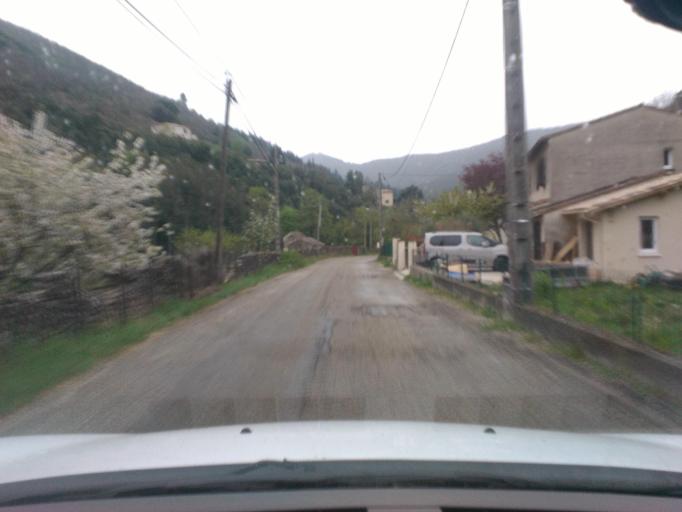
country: FR
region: Languedoc-Roussillon
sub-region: Departement du Gard
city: Valleraugue
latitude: 44.0901
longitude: 3.6383
